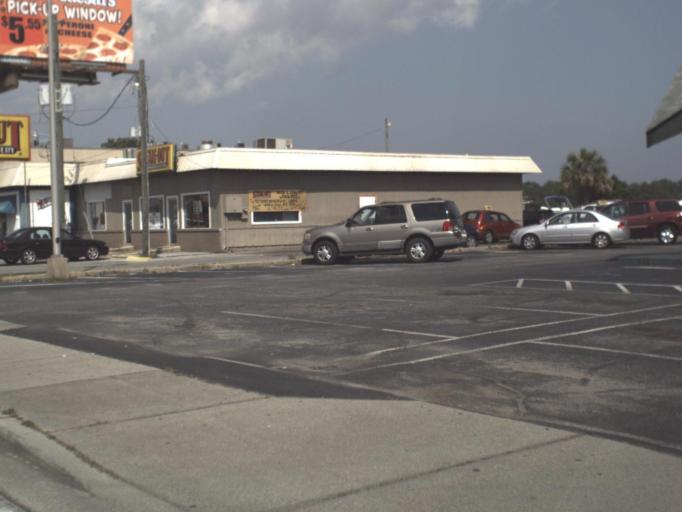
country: US
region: Florida
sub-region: Escambia County
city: Ferry Pass
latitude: 30.4892
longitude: -87.1960
